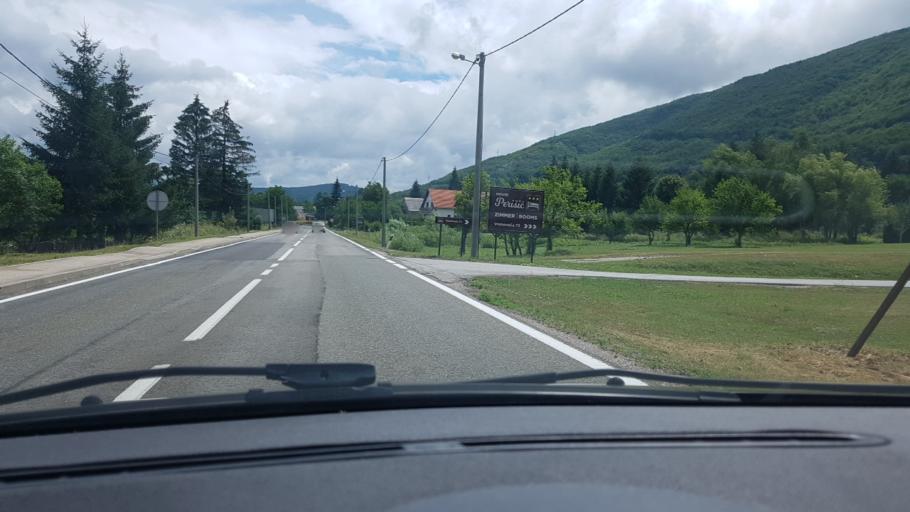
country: HR
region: Licko-Senjska
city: Jezerce
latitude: 44.7633
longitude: 15.6917
